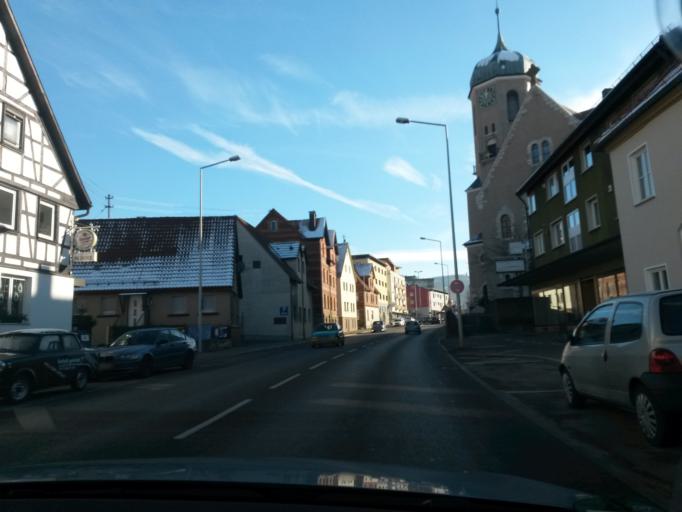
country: DE
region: Baden-Wuerttemberg
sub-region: Regierungsbezirk Stuttgart
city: Geislingen an der Steige
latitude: 48.6270
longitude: 9.8217
